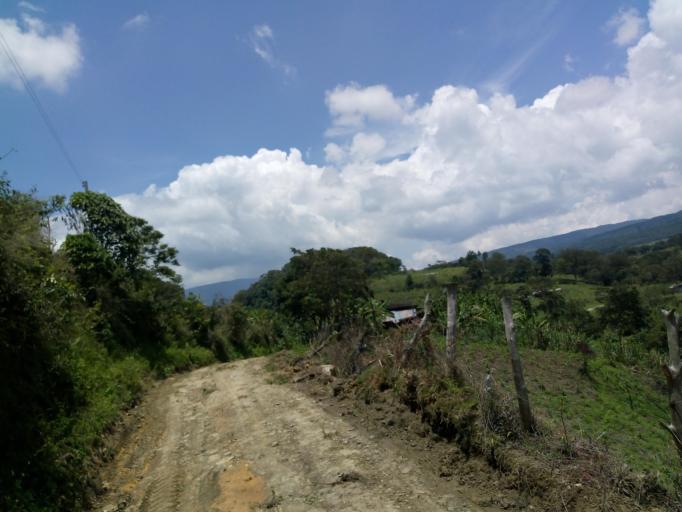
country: CO
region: Boyaca
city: Moniquira
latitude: 5.8696
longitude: -73.5080
